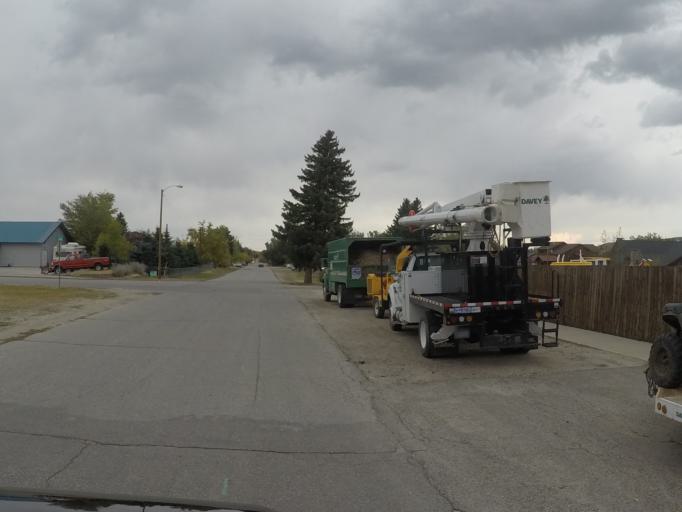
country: US
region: Montana
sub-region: Carbon County
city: Red Lodge
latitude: 45.1925
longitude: -109.2445
